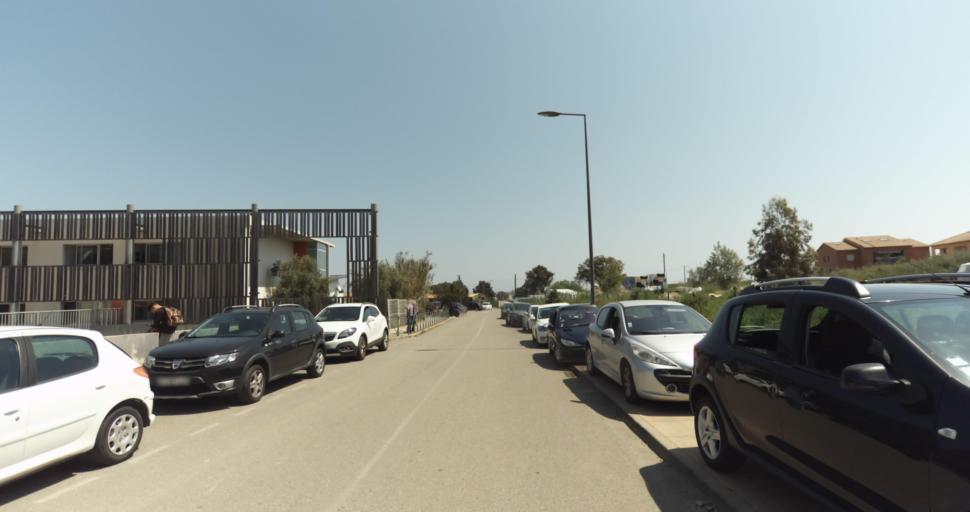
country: FR
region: Corsica
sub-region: Departement de la Haute-Corse
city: Biguglia
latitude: 42.5969
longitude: 9.4368
